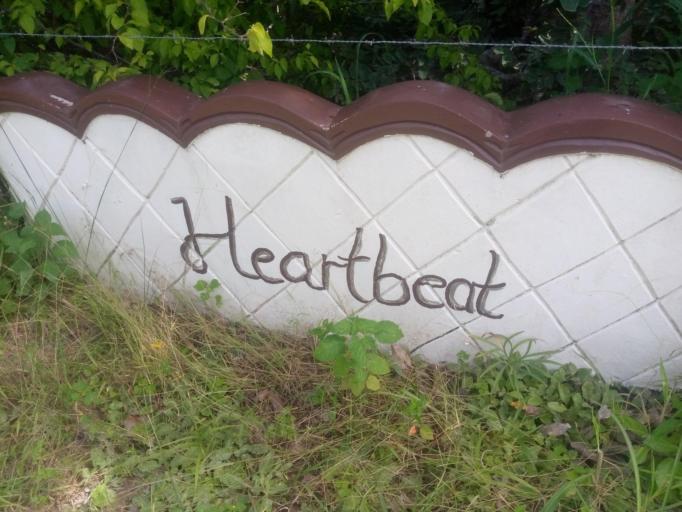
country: GM
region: Western
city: Gunjur
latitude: 13.0302
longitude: -16.7293
